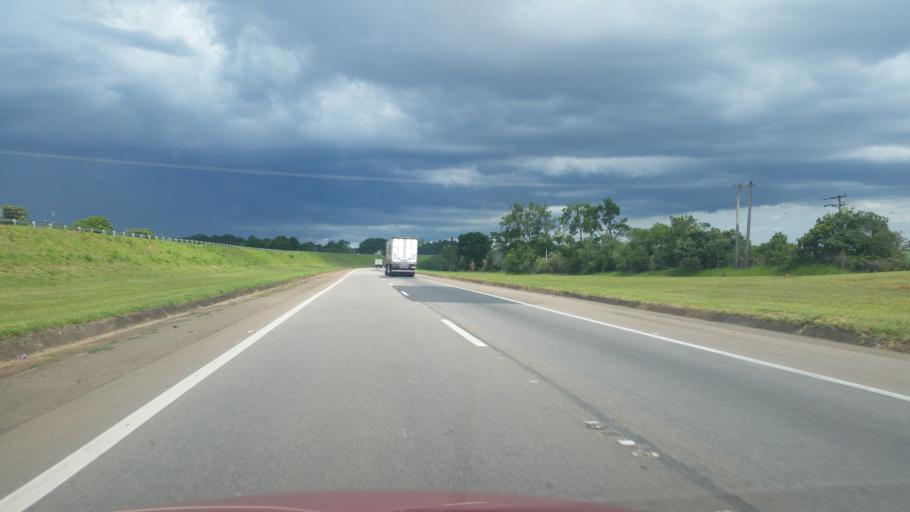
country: BR
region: Sao Paulo
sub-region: Boituva
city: Boituva
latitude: -23.2947
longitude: -47.6984
